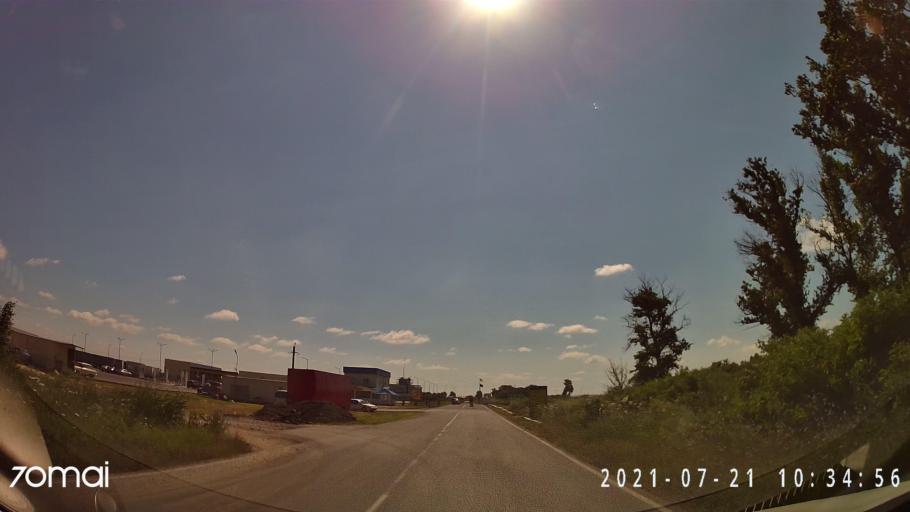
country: RO
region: Tulcea
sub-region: Oras Isaccea
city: Isaccea
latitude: 45.2931
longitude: 28.4554
